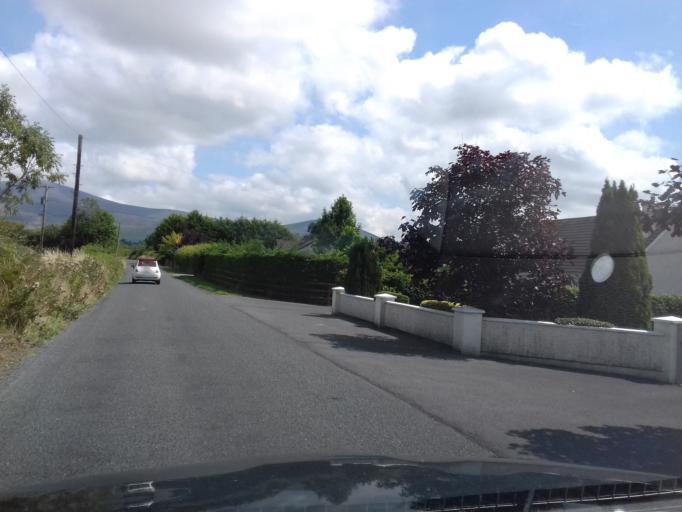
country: IE
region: Leinster
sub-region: Kilkenny
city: Graiguenamanagh
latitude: 52.6073
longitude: -6.8873
